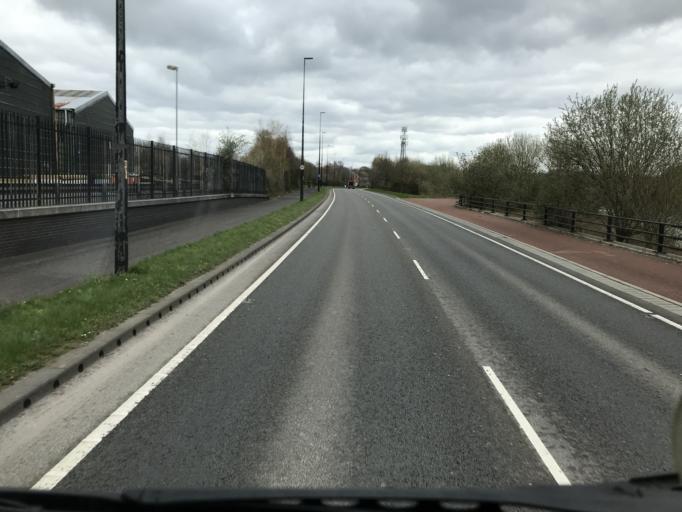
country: GB
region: England
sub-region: Trafford
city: Partington
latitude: 53.4209
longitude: -2.4384
